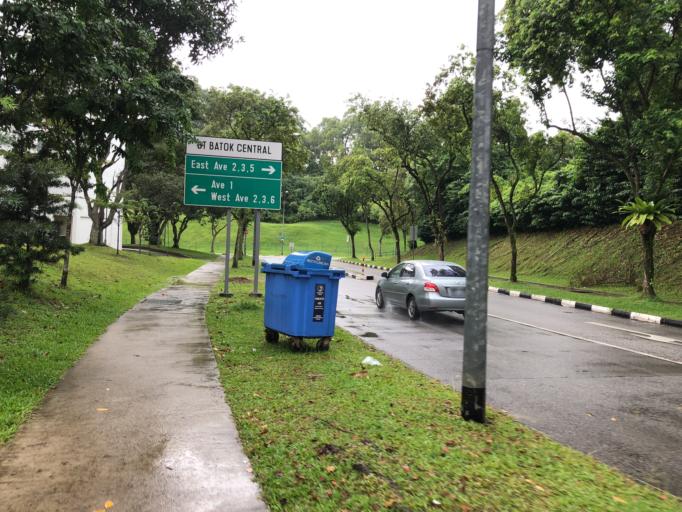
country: SG
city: Singapore
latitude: 1.3470
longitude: 103.7504
